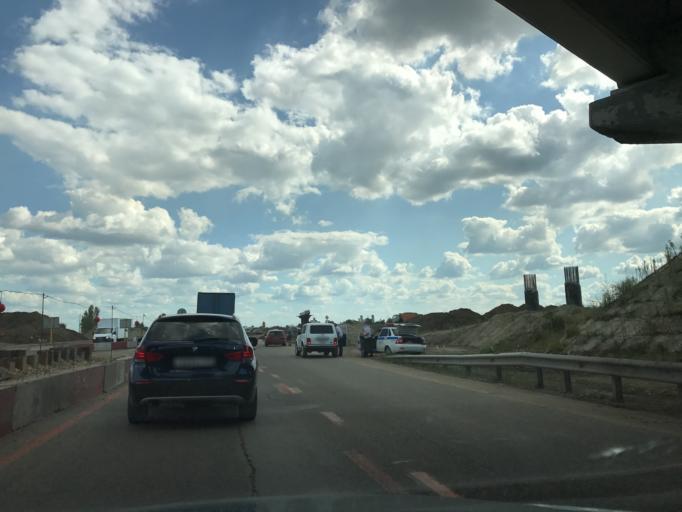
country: RU
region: Adygeya
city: Tlyustenkhabl'
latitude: 44.9505
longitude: 39.1239
